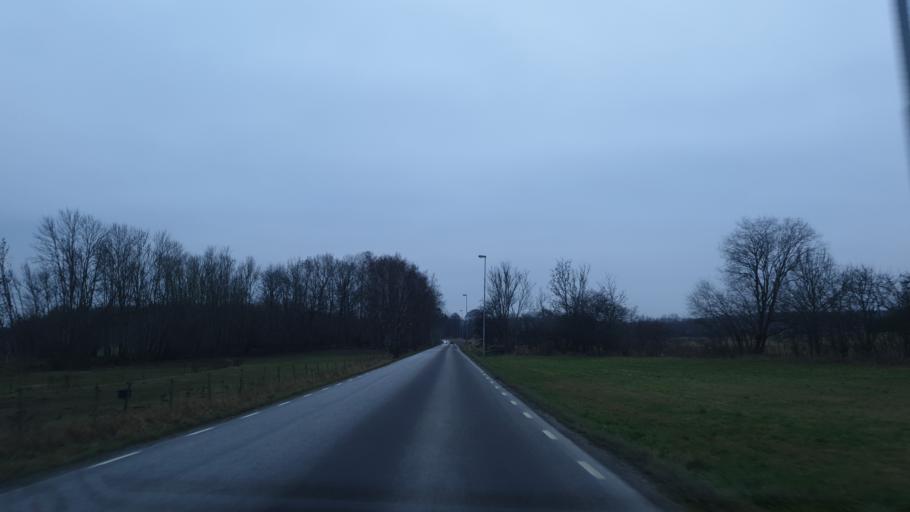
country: SE
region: Blekinge
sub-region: Karlskrona Kommun
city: Rodeby
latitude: 56.2160
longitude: 15.6676
